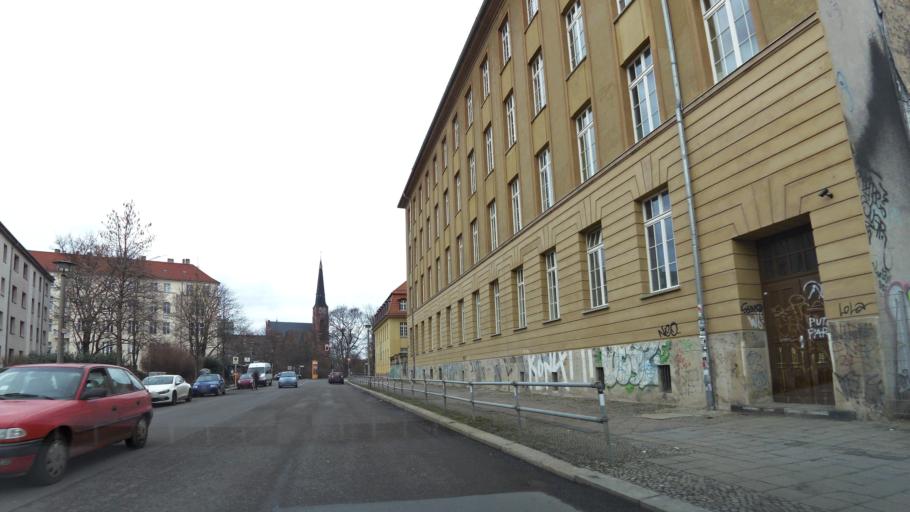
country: DE
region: Berlin
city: Treptow Bezirk
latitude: 52.5019
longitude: 13.4578
